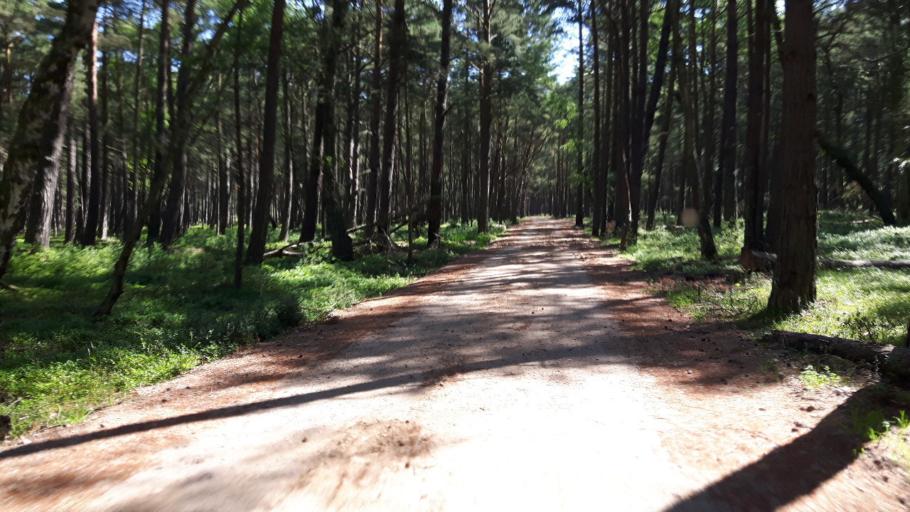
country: PL
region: Pomeranian Voivodeship
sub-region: Powiat slupski
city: Smoldzino
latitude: 54.6733
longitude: 17.1085
